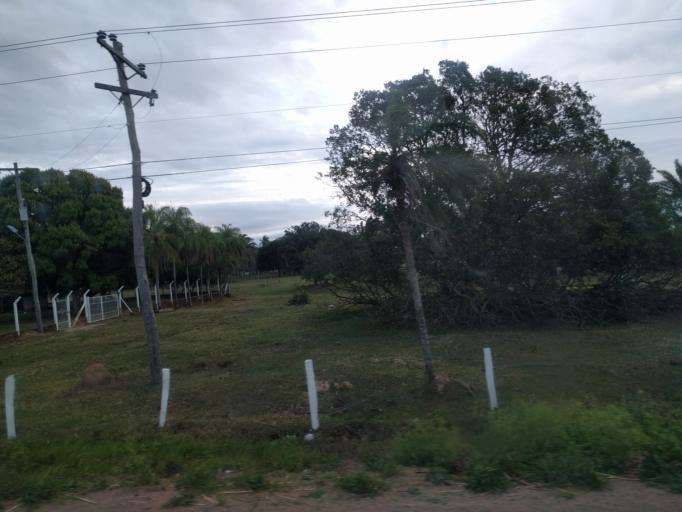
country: BO
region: Santa Cruz
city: Warnes
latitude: -17.4710
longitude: -63.1857
